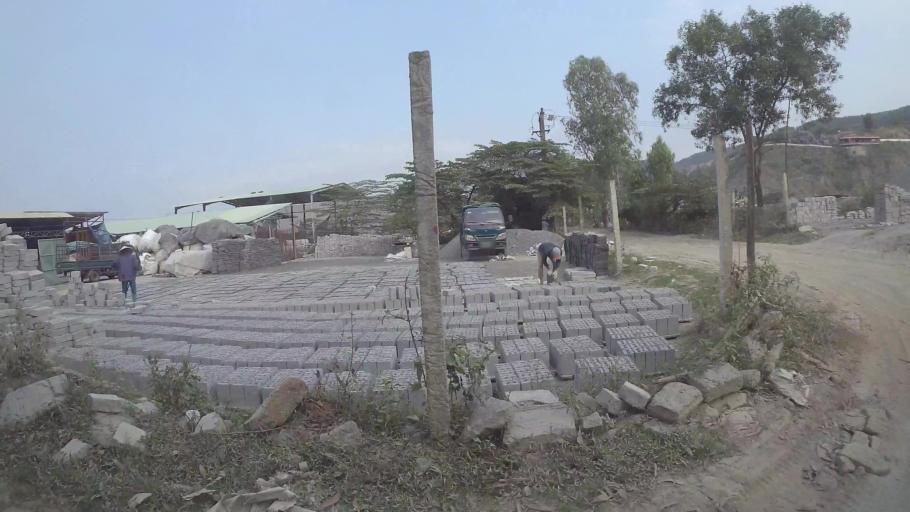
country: VN
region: Da Nang
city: Lien Chieu
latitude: 16.0446
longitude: 108.1461
